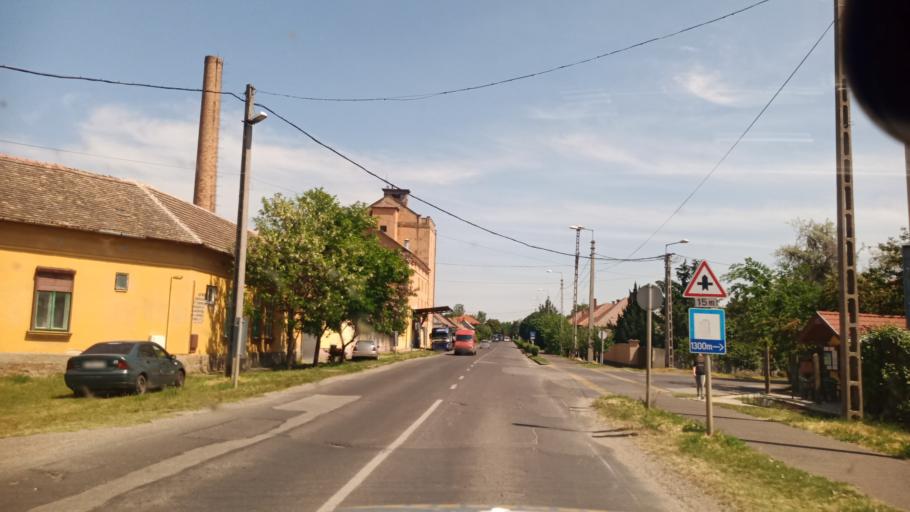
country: HU
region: Bekes
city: Oroshaza
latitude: 46.5585
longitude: 20.6519
